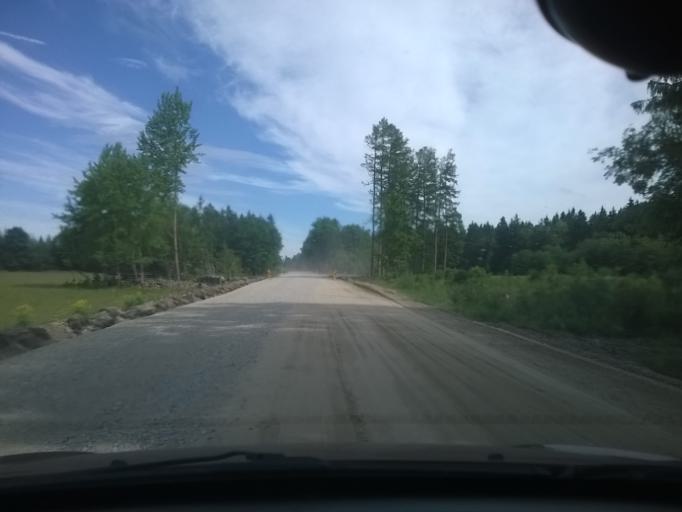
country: EE
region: Harju
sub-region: Raasiku vald
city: Raasiku
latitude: 59.2844
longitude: 25.1967
